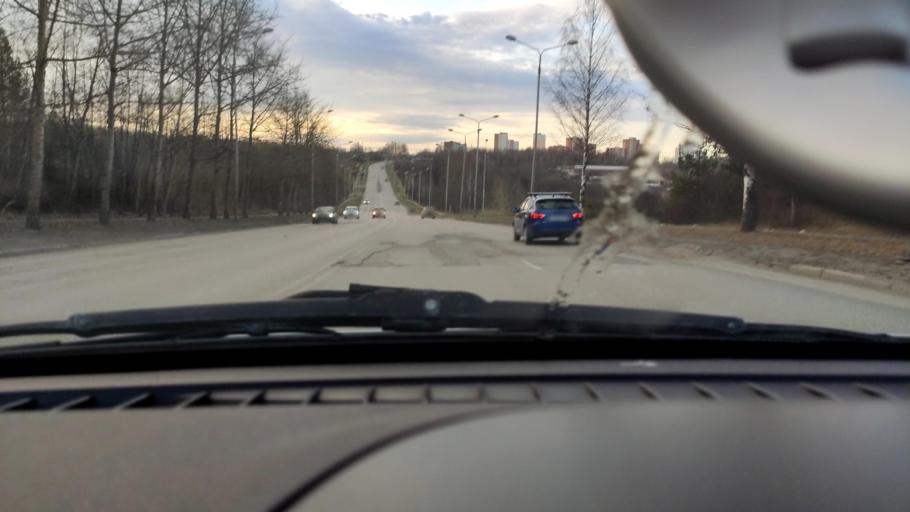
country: RU
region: Perm
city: Perm
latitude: 58.0736
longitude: 56.3681
